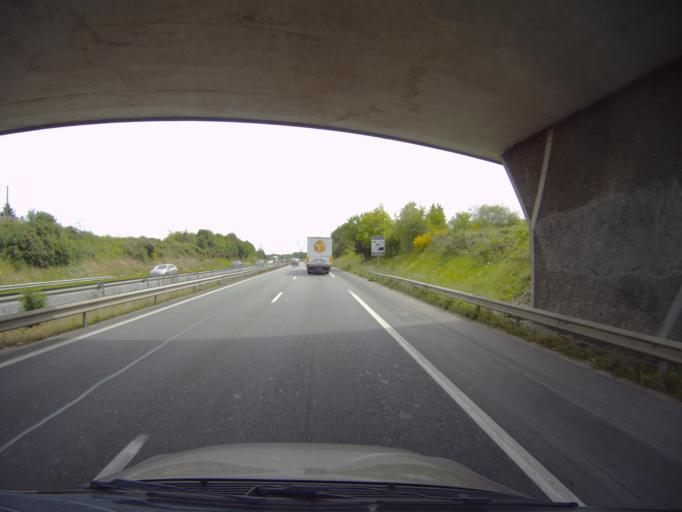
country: FR
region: Pays de la Loire
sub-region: Departement de la Loire-Atlantique
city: Les Sorinieres
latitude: 47.1597
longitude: -1.5345
